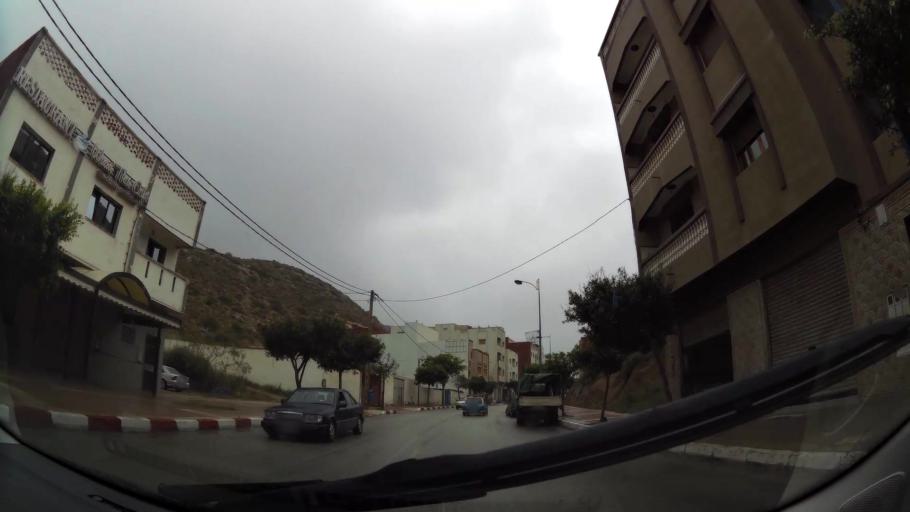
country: MA
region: Taza-Al Hoceima-Taounate
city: Al Hoceima
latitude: 35.2524
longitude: -3.9436
